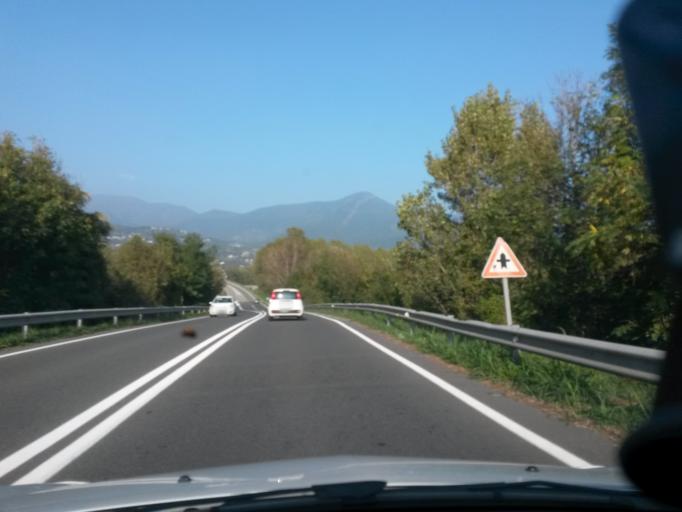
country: IT
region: Piedmont
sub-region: Provincia di Torino
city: Sant'Ambrogio di Torino
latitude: 45.0970
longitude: 7.3714
